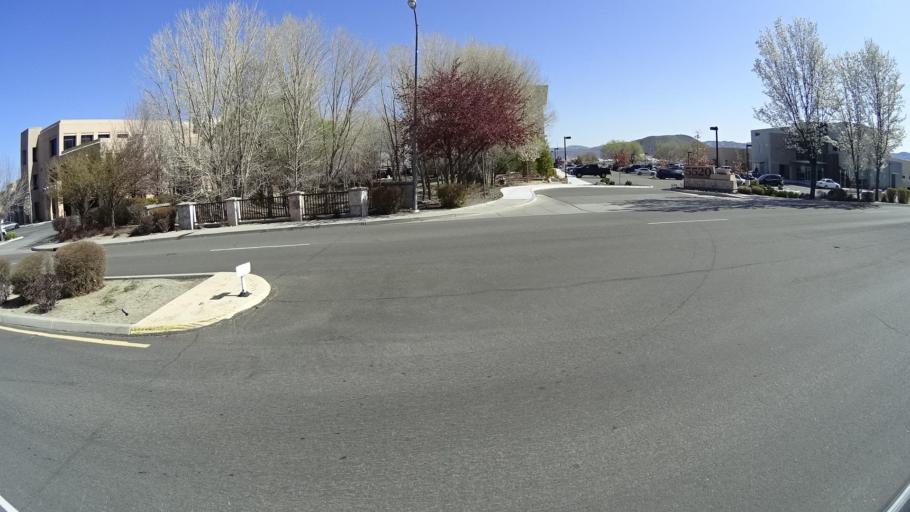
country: US
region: Nevada
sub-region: Washoe County
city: Reno
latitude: 39.4640
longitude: -119.7893
